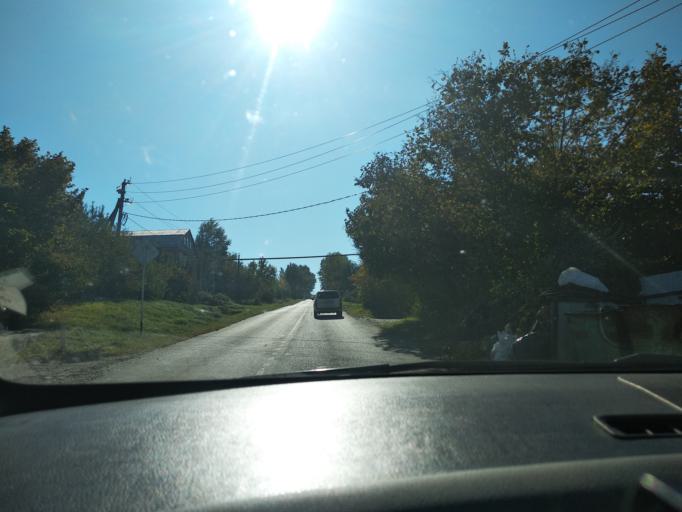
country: RU
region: Krasnodarskiy
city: Goryachiy Klyuch
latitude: 44.6261
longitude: 39.1572
